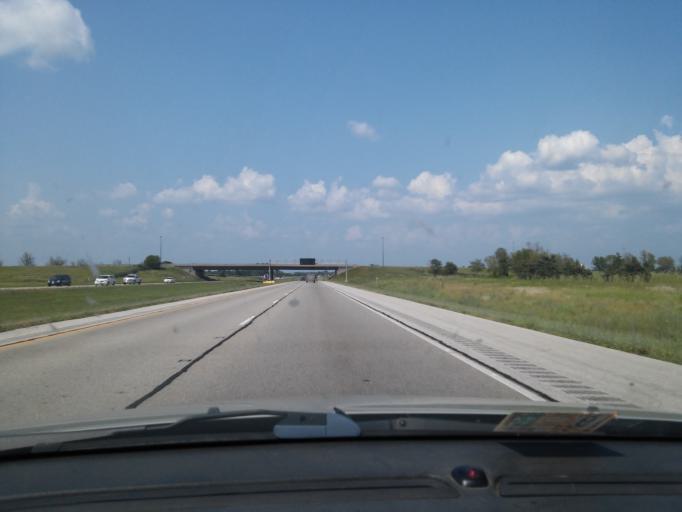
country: US
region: Illinois
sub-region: McLean County
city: Twin Grove
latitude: 40.4058
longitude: -89.0553
